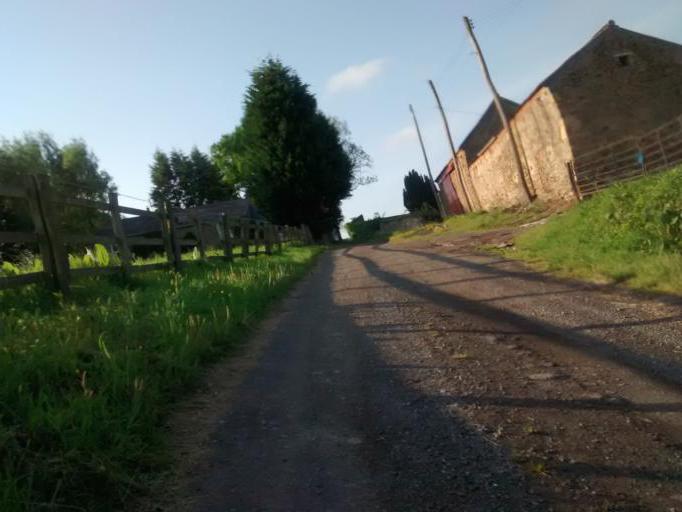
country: GB
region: England
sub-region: County Durham
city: West Cornforth
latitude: 54.7269
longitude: -1.5474
